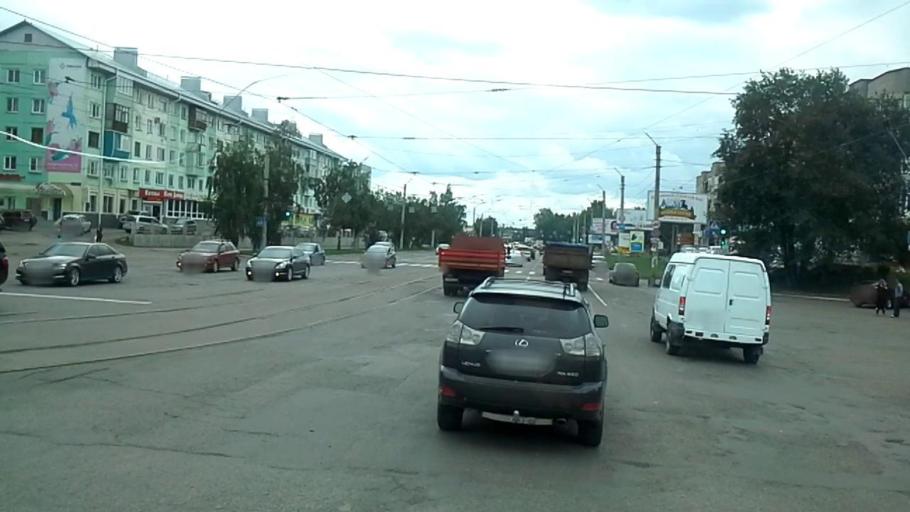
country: RU
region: Altai Krai
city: Biysk
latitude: 52.5434
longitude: 85.2176
